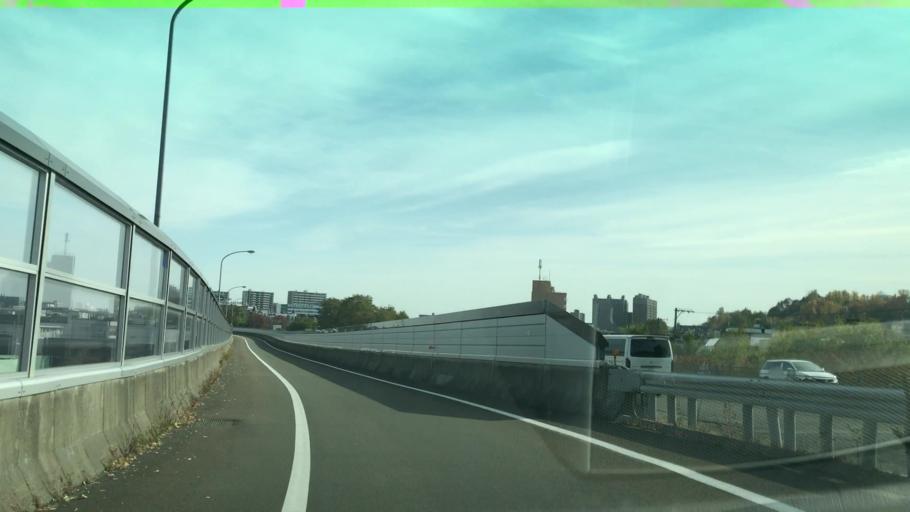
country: JP
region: Hokkaido
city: Sapporo
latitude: 43.0914
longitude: 141.2626
